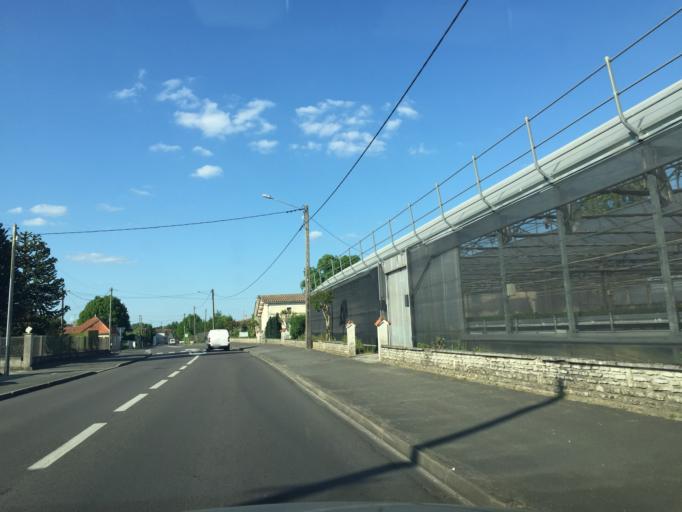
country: FR
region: Aquitaine
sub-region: Departement de la Gironde
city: Les Peintures
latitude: 45.0647
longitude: -0.0957
